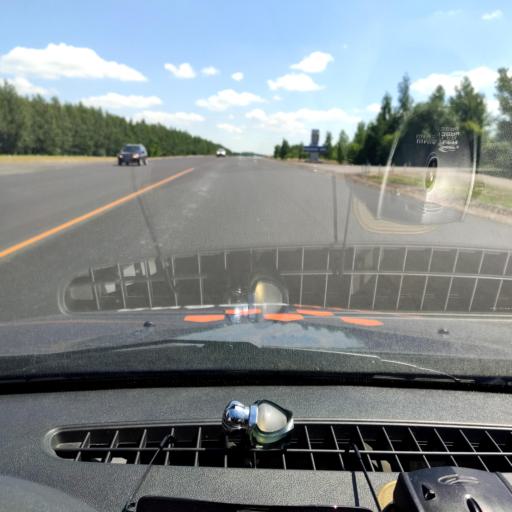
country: RU
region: Orjol
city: Zmiyevka
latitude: 52.8030
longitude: 36.3000
